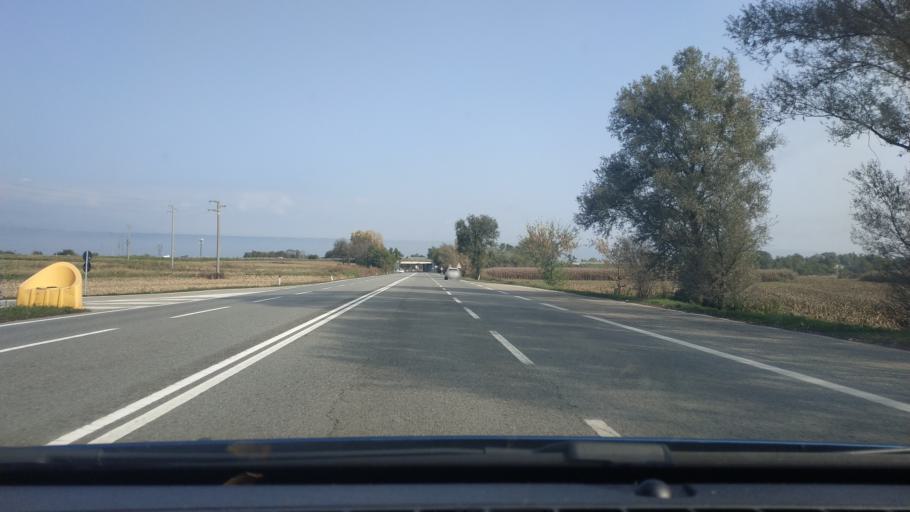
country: IT
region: Piedmont
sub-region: Provincia di Torino
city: Romano Canavese
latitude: 45.4178
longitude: 7.8853
